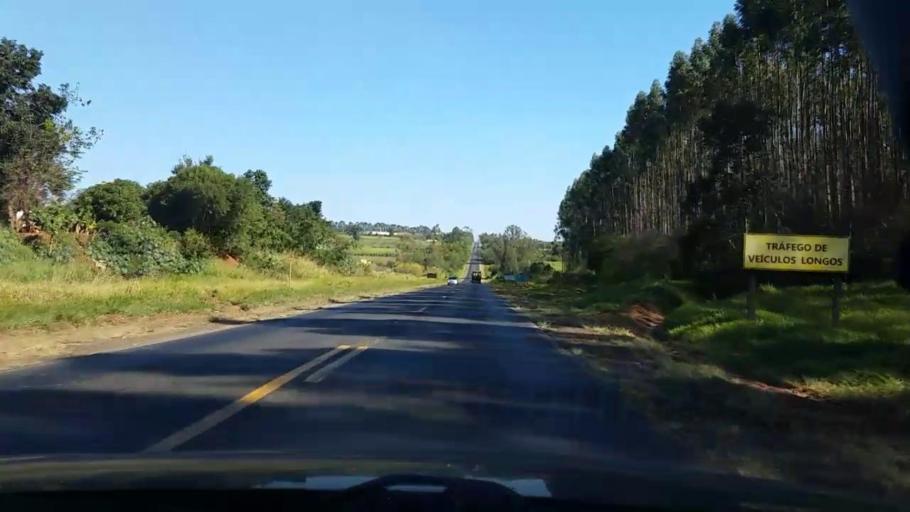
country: BR
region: Sao Paulo
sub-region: Sao Manuel
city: Sao Manuel
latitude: -22.8078
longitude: -48.6731
